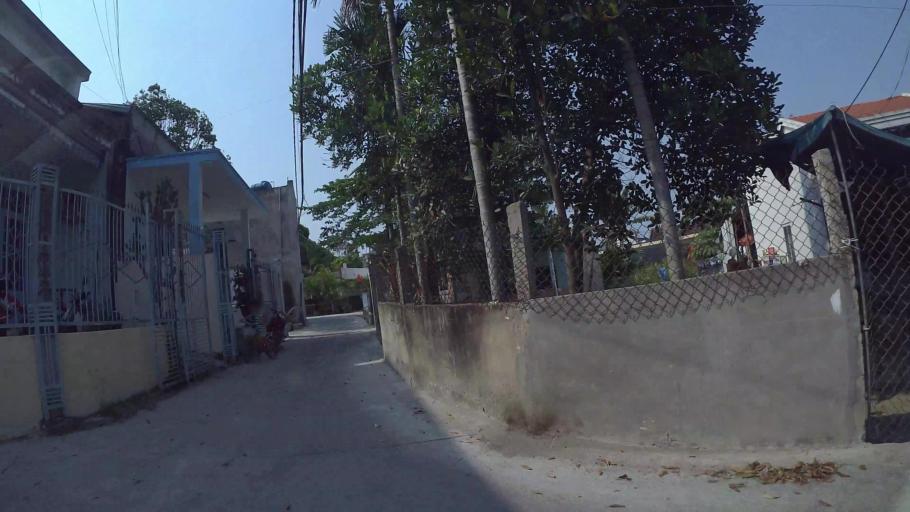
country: VN
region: Da Nang
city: Cam Le
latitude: 16.0033
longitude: 108.1924
